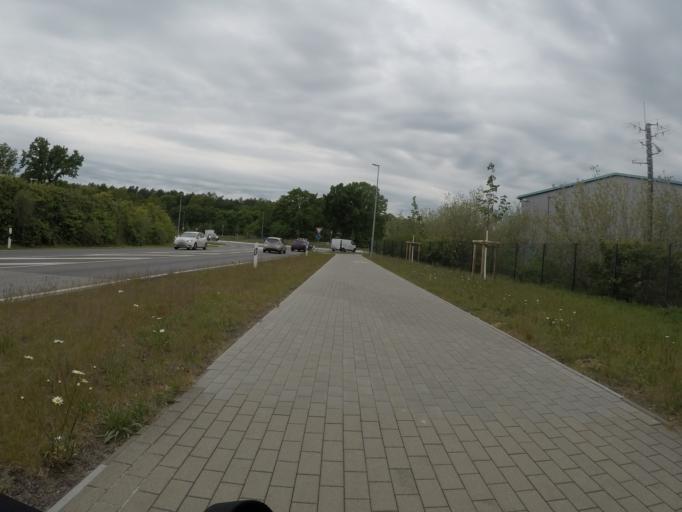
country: DE
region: Schleswig-Holstein
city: Norderstedt
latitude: 53.7230
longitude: 9.9855
